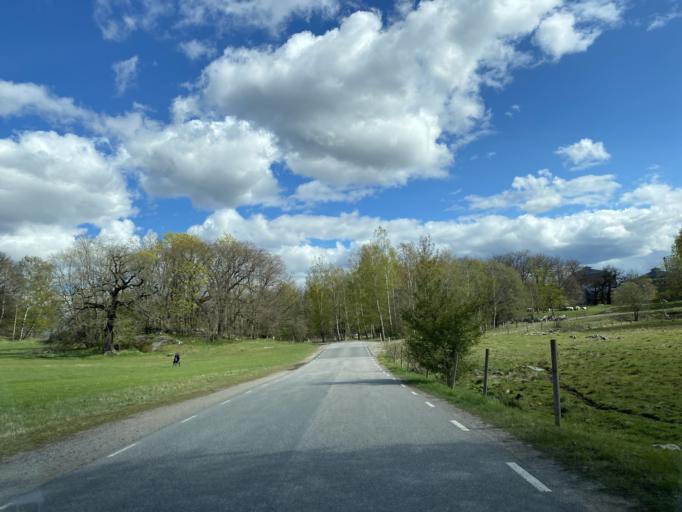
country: SE
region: Stockholm
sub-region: Stockholms Kommun
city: OEstermalm
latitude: 59.3630
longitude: 18.0871
